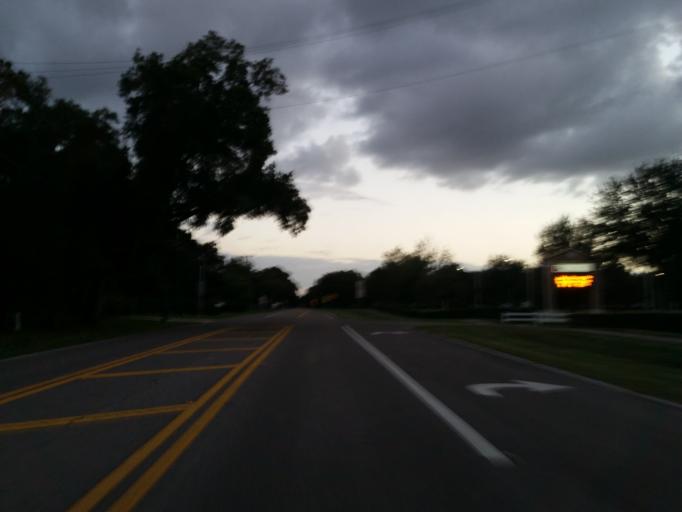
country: US
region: Florida
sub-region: Hillsborough County
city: Brandon
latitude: 27.9103
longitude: -82.2693
